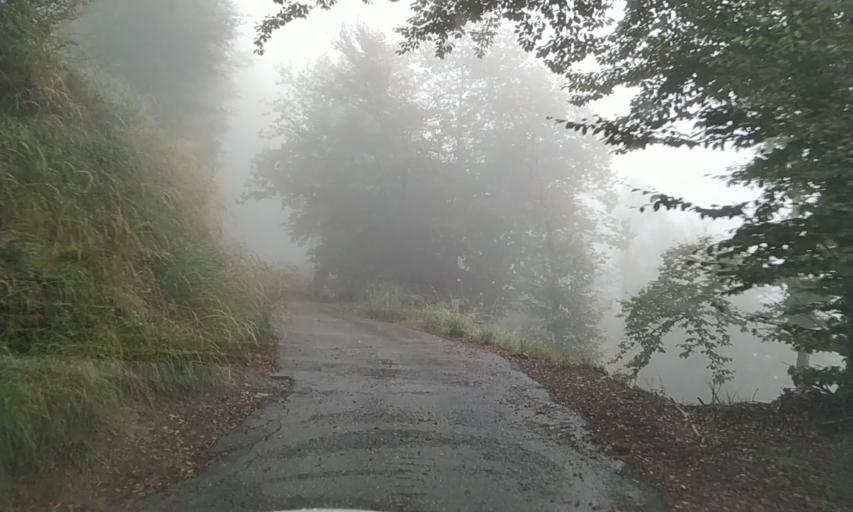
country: IT
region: Piedmont
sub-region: Provincia di Vercelli
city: Civiasco
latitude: 45.8299
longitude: 8.3001
